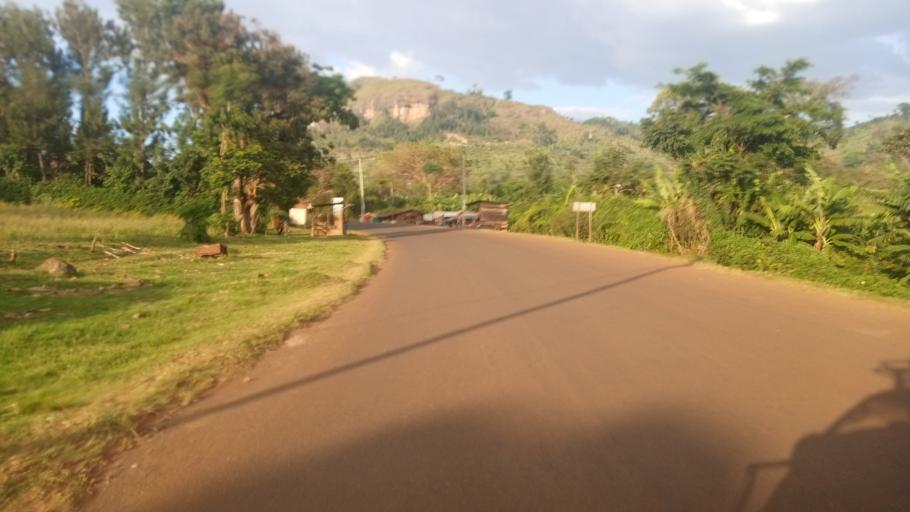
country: UG
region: Eastern Region
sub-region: Kapchorwa District
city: Kapchorwa
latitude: 1.3264
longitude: 34.3557
